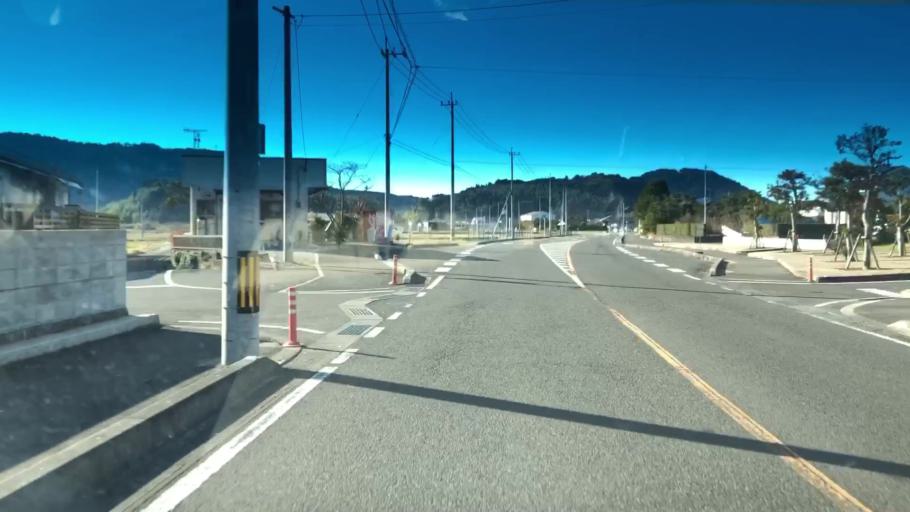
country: JP
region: Kagoshima
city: Satsumasendai
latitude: 31.8167
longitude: 130.2839
